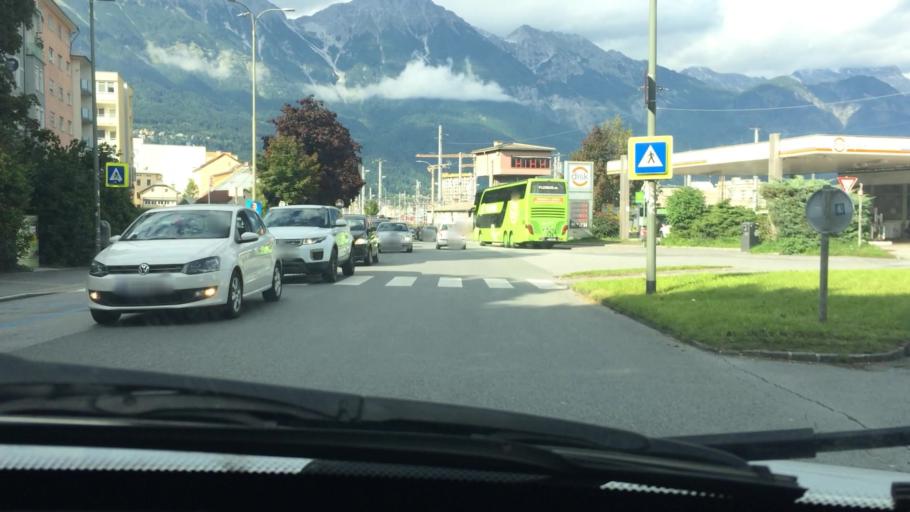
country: AT
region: Tyrol
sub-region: Innsbruck Stadt
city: Innsbruck
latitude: 47.2581
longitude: 11.3996
